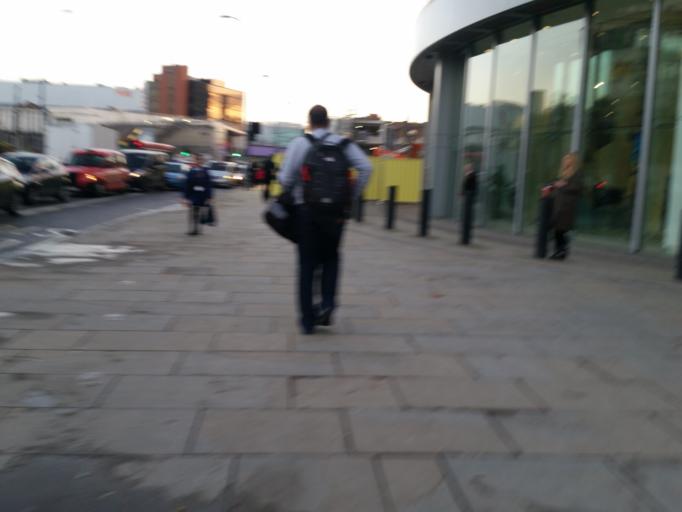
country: GB
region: England
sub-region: Greater London
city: Hammersmith
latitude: 51.5113
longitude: -0.2248
